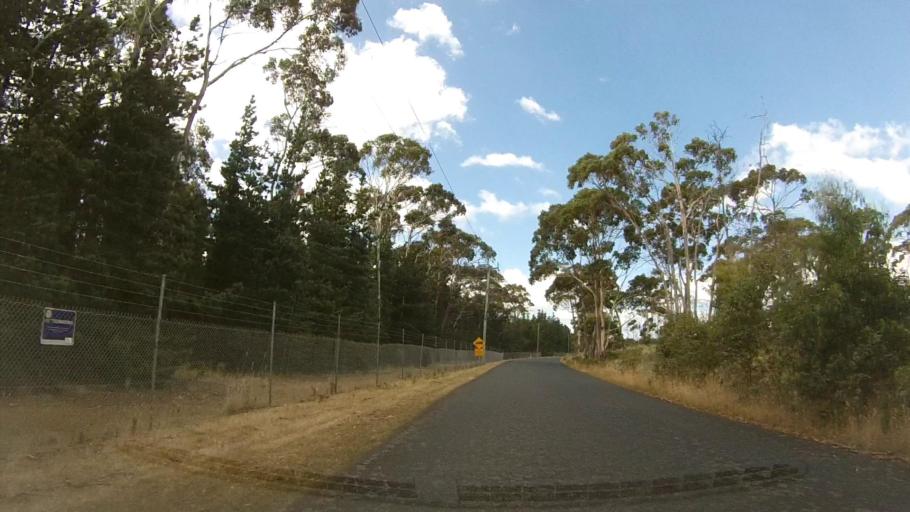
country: AU
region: Tasmania
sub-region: Clarence
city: Seven Mile Beach
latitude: -42.8449
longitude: 147.5295
